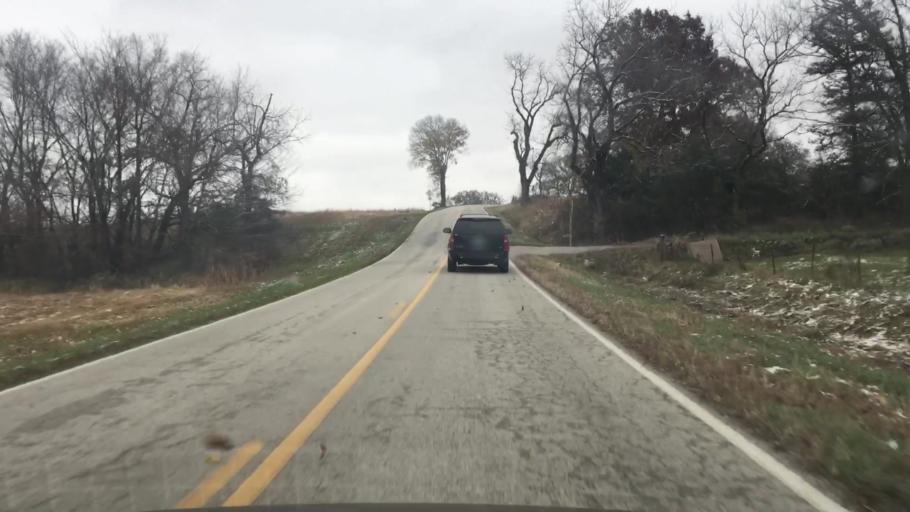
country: US
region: Missouri
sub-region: Saint Clair County
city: Osceola
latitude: 37.9897
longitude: -93.6258
